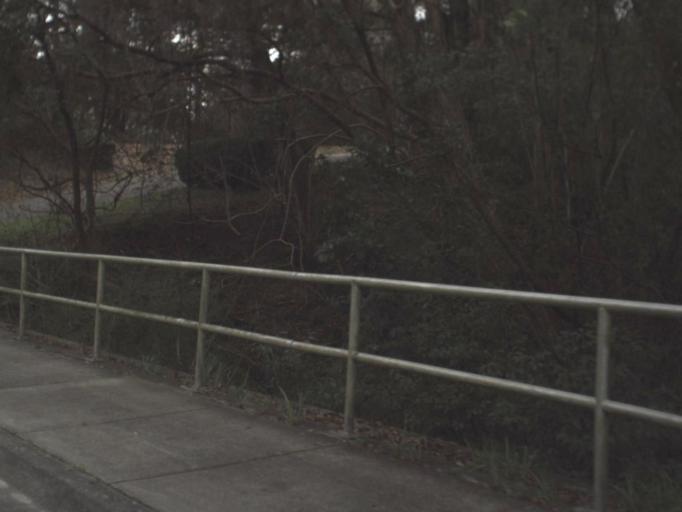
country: US
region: Florida
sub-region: Leon County
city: Tallahassee
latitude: 30.4849
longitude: -84.2773
